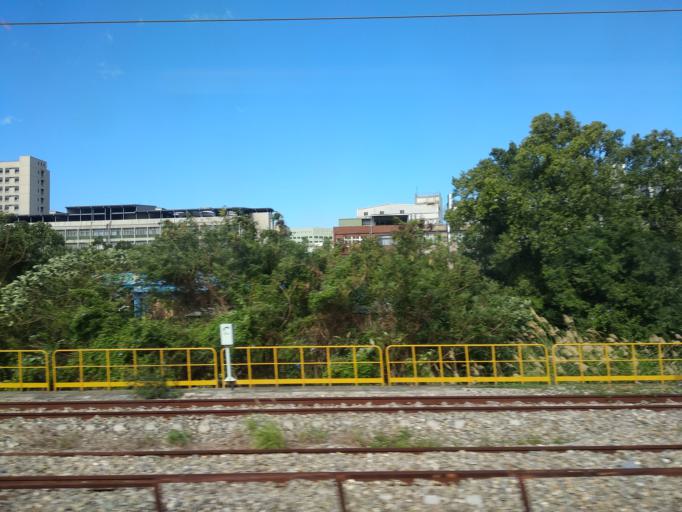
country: TW
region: Taiwan
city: Taoyuan City
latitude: 24.9772
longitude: 121.2705
